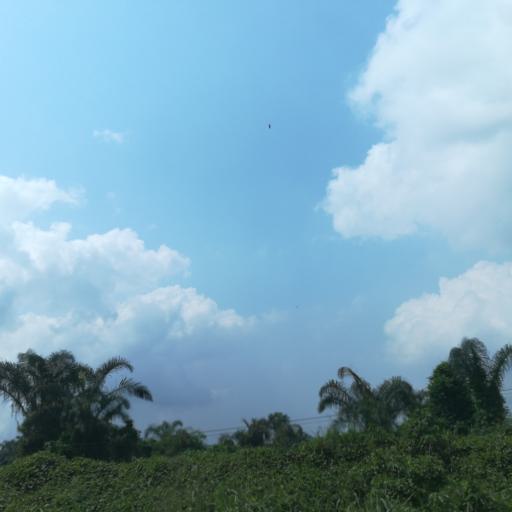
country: NG
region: Rivers
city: Okrika
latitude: 4.8075
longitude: 7.1010
